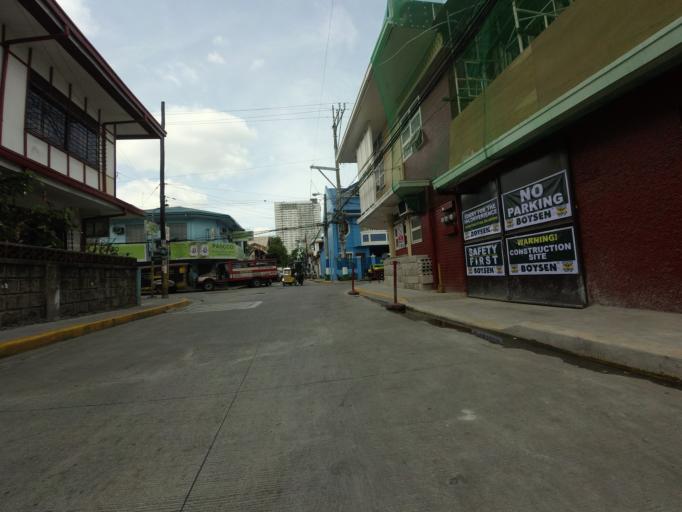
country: PH
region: Metro Manila
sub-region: City of Manila
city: Quiapo
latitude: 14.5800
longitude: 120.9958
